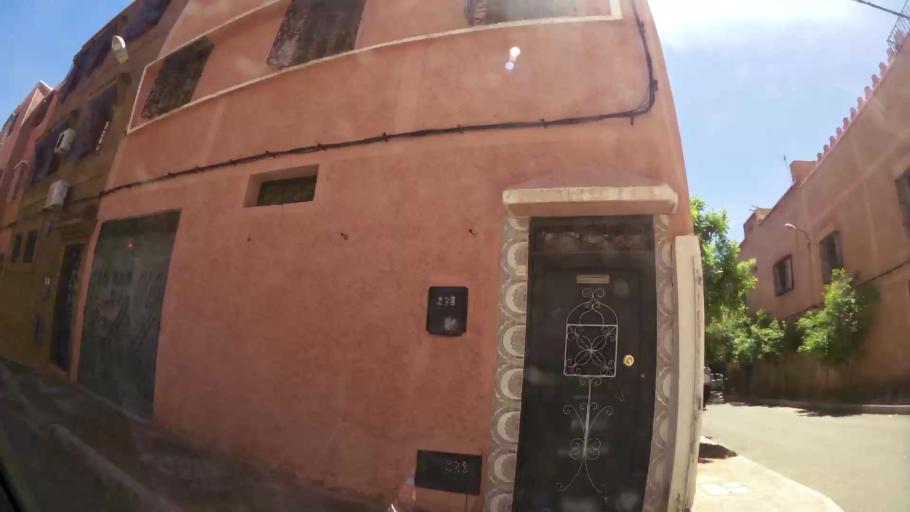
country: MA
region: Marrakech-Tensift-Al Haouz
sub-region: Marrakech
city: Marrakesh
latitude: 31.6528
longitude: -8.0007
